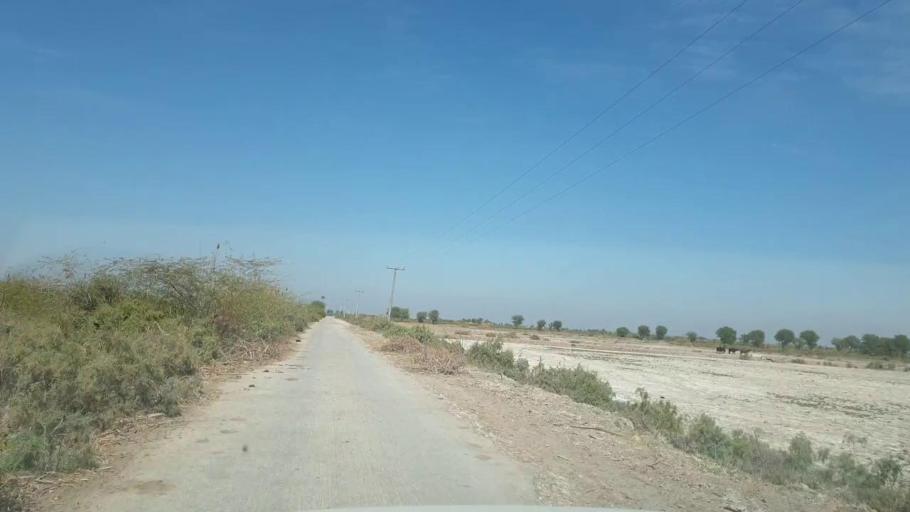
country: PK
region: Sindh
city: Pithoro
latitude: 25.6183
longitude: 69.2159
